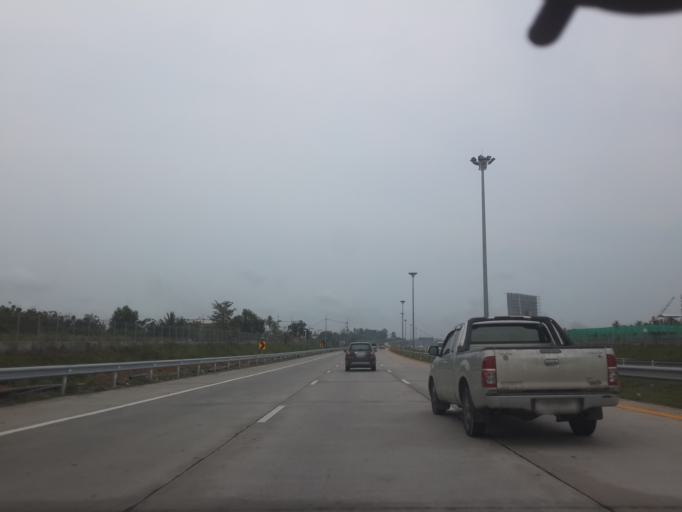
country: TH
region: Chon Buri
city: Phatthaya
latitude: 12.9512
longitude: 100.9428
